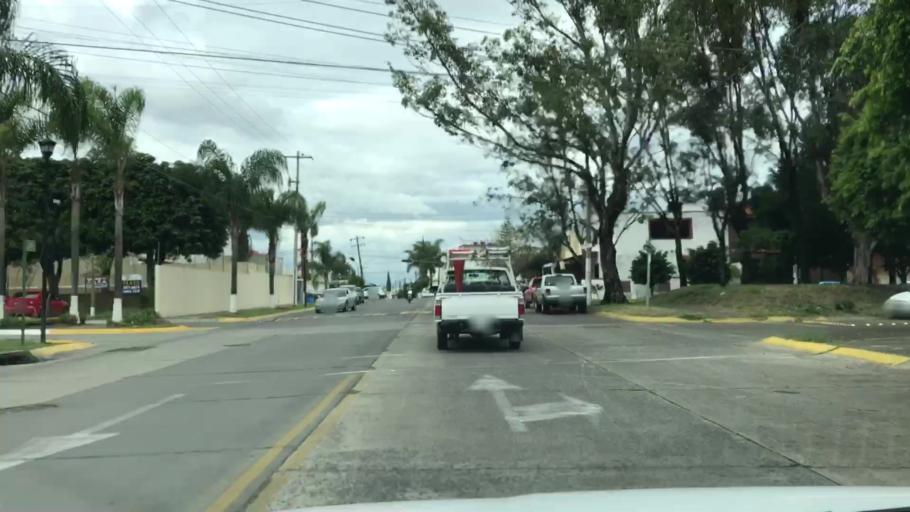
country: MX
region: Jalisco
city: Guadalajara
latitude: 20.6412
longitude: -103.4380
